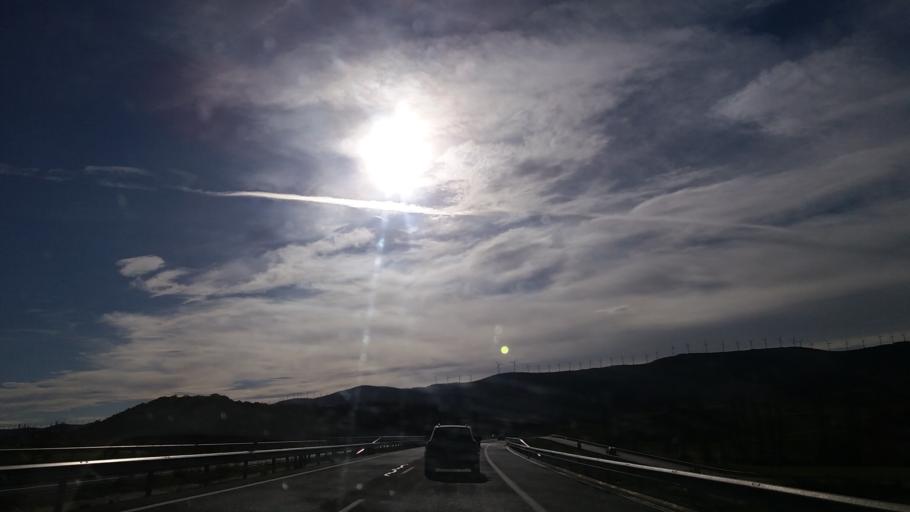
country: ES
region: Navarre
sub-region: Provincia de Navarra
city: Monreal
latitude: 42.6936
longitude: -1.4803
